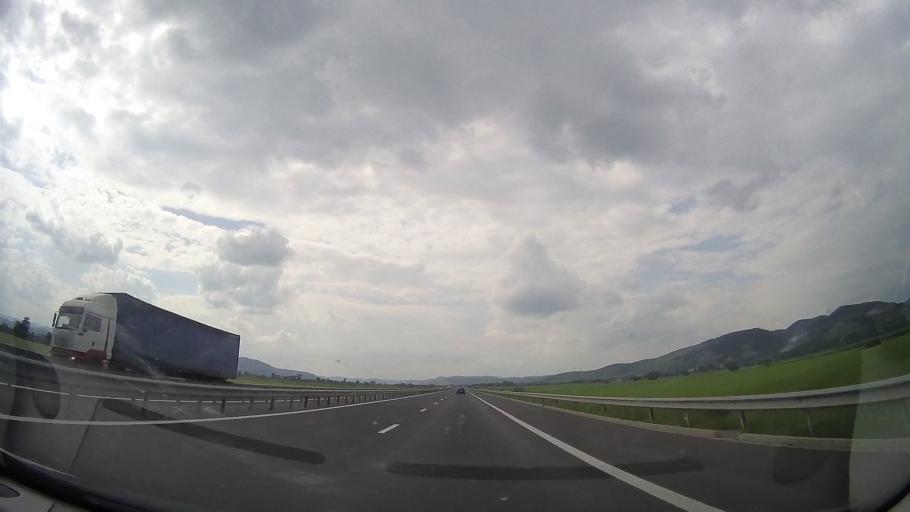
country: RO
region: Hunedoara
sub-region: Oras Simeria
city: Simeria
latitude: 45.8757
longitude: 23.0052
